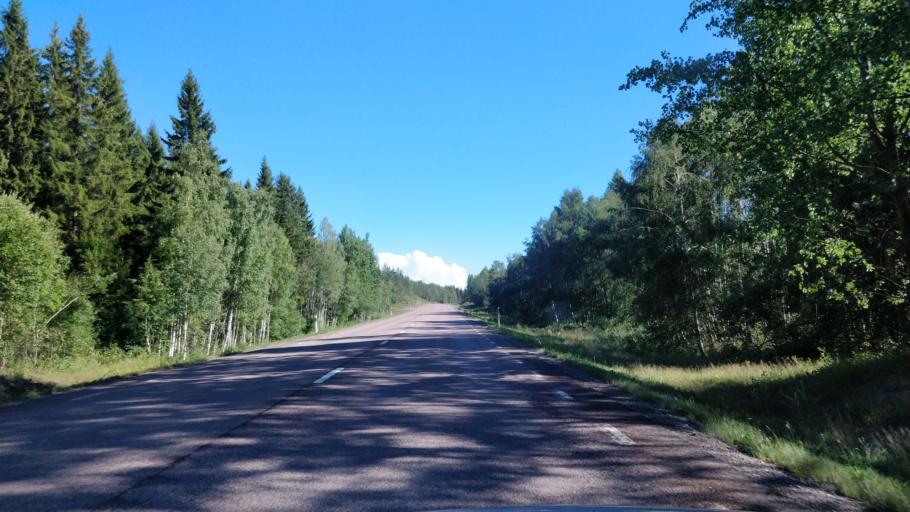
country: SE
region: Dalarna
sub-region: Faluns Kommun
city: Falun
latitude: 60.6494
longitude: 15.5639
